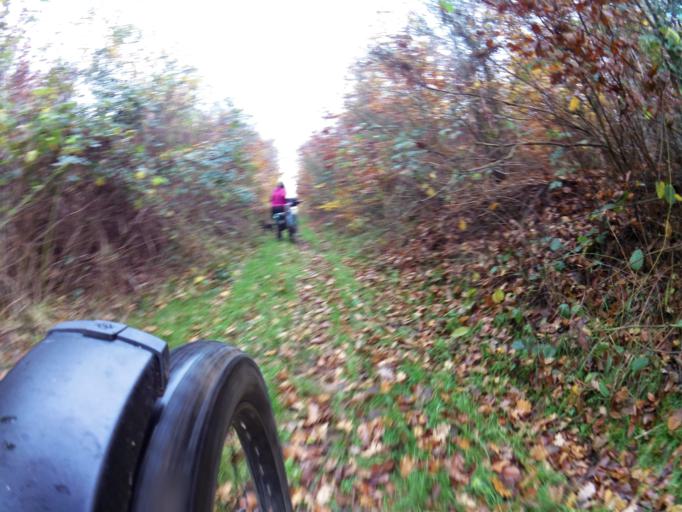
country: PL
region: Pomeranian Voivodeship
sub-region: Powiat pucki
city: Krokowa
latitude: 54.7309
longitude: 18.1321
